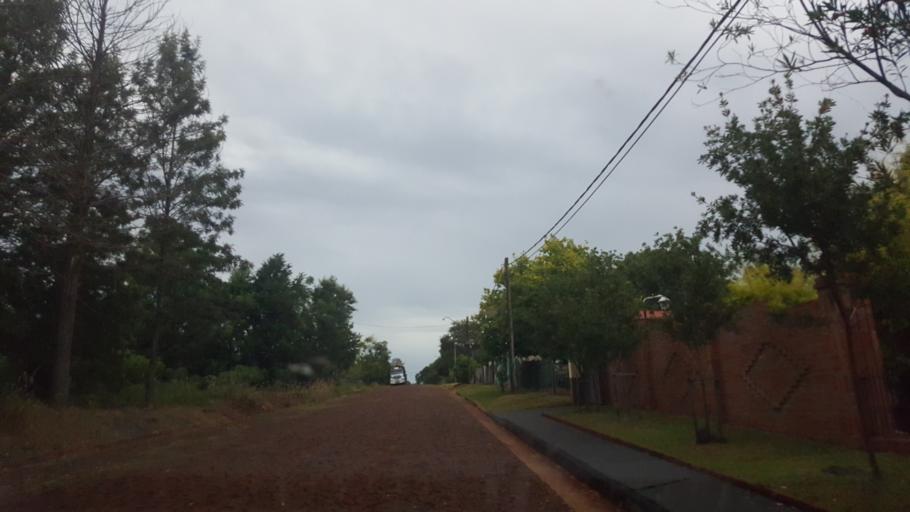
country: AR
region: Misiones
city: Capiovi
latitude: -26.9286
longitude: -55.0498
